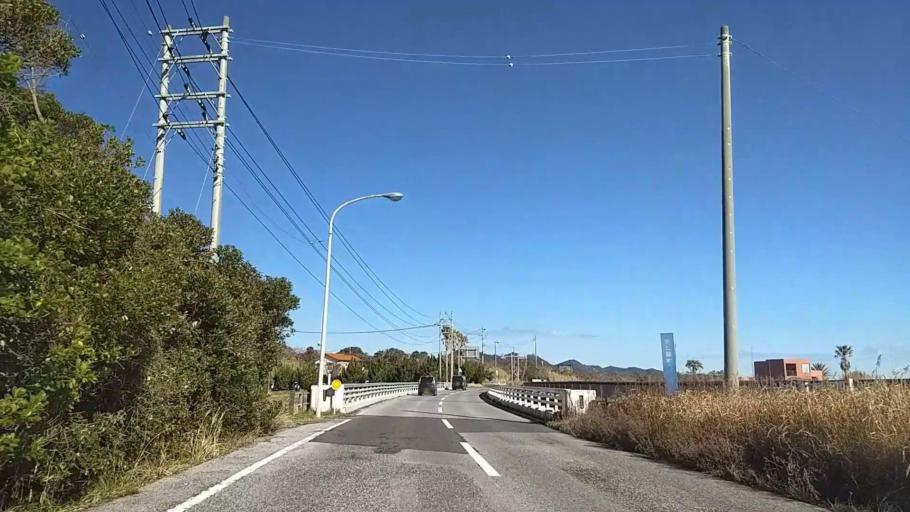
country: JP
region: Chiba
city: Tateyama
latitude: 35.0101
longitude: 139.9776
